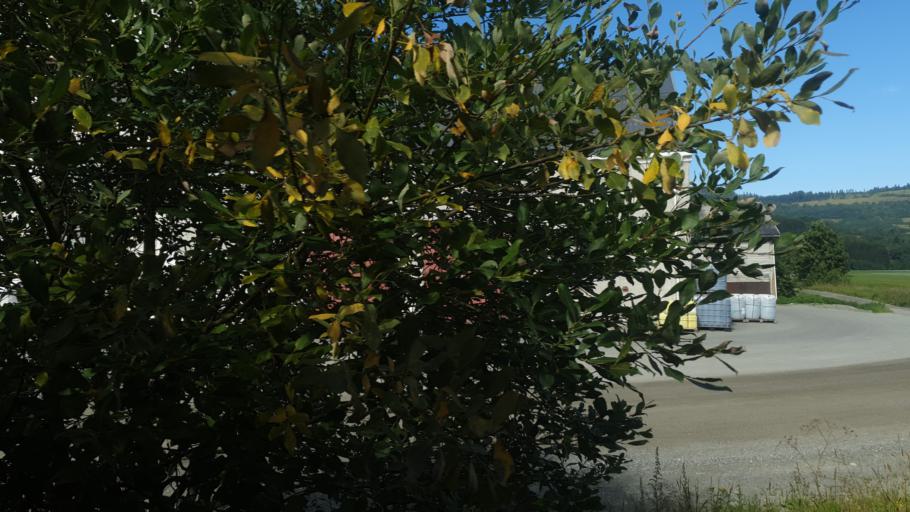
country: NO
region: Sor-Trondelag
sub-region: Orkdal
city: Orkanger
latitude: 63.2680
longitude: 9.8151
